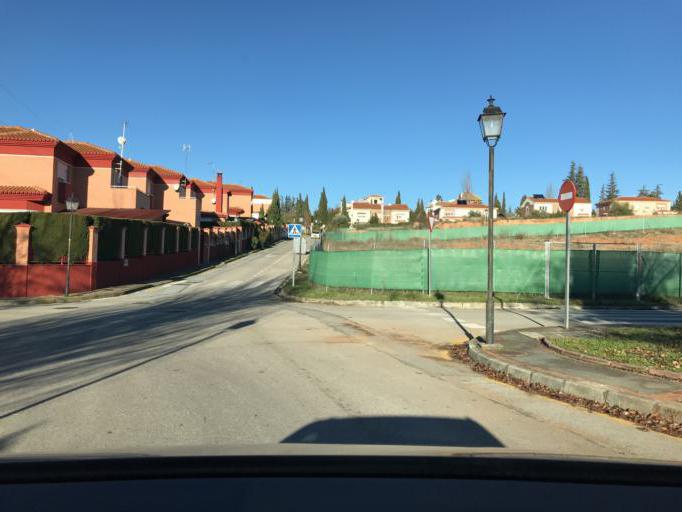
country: ES
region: Andalusia
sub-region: Provincia de Granada
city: Albolote
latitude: 37.2486
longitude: -3.6490
